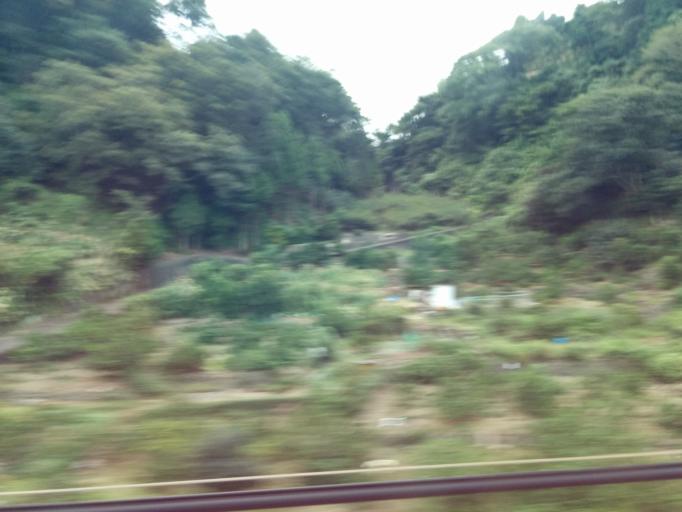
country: JP
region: Shizuoka
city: Shizuoka-shi
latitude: 34.9196
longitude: 138.3572
